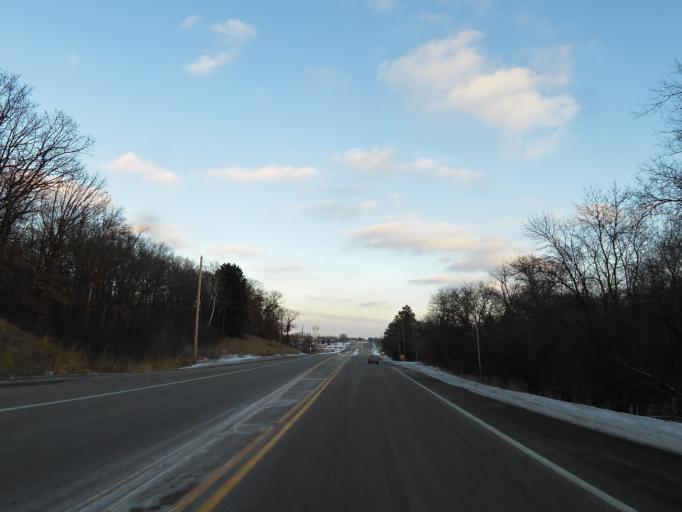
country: US
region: Minnesota
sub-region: Dakota County
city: Lakeville
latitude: 44.6452
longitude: -93.3079
